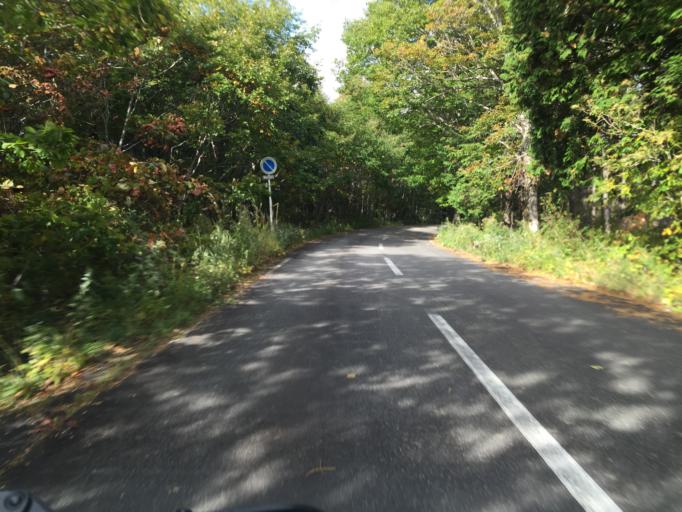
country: JP
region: Fukushima
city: Inawashiro
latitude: 37.6525
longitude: 140.2432
